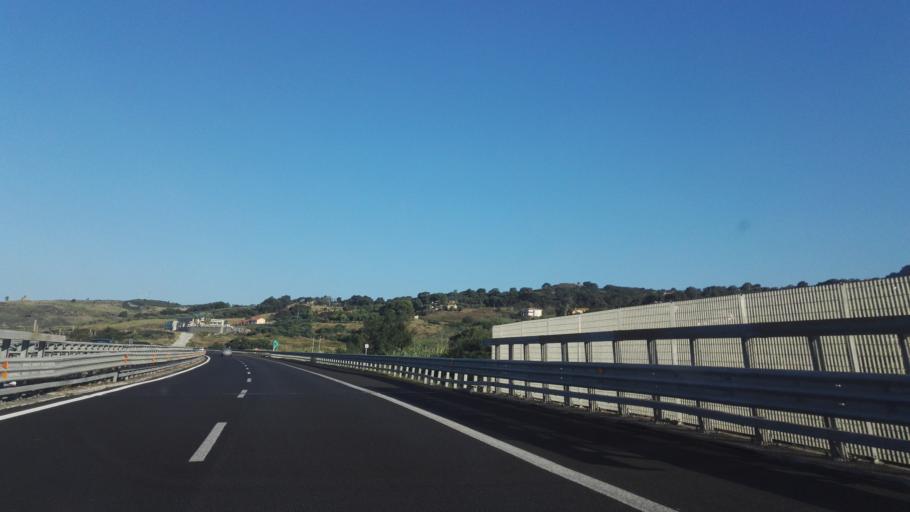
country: IT
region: Calabria
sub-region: Provincia di Catanzaro
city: Gizzeria
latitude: 38.9477
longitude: 16.1855
